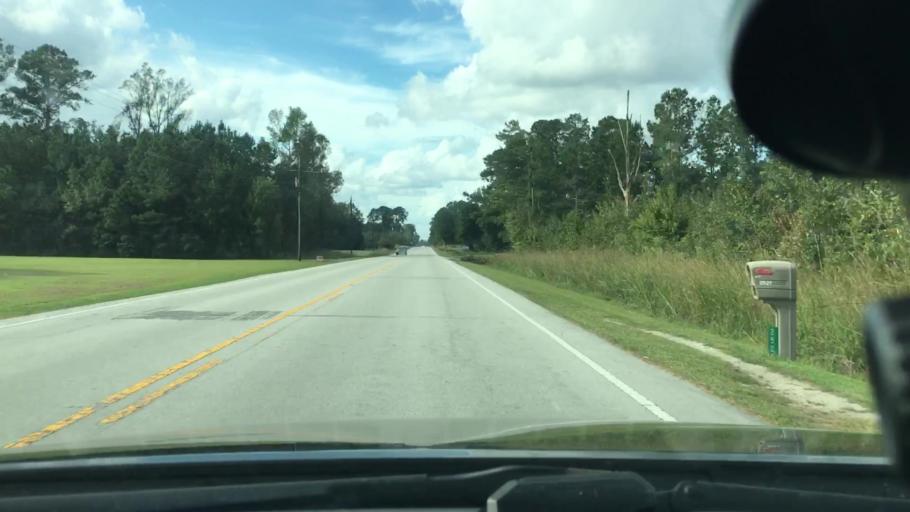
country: US
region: North Carolina
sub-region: Craven County
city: Vanceboro
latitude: 35.3547
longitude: -77.1916
